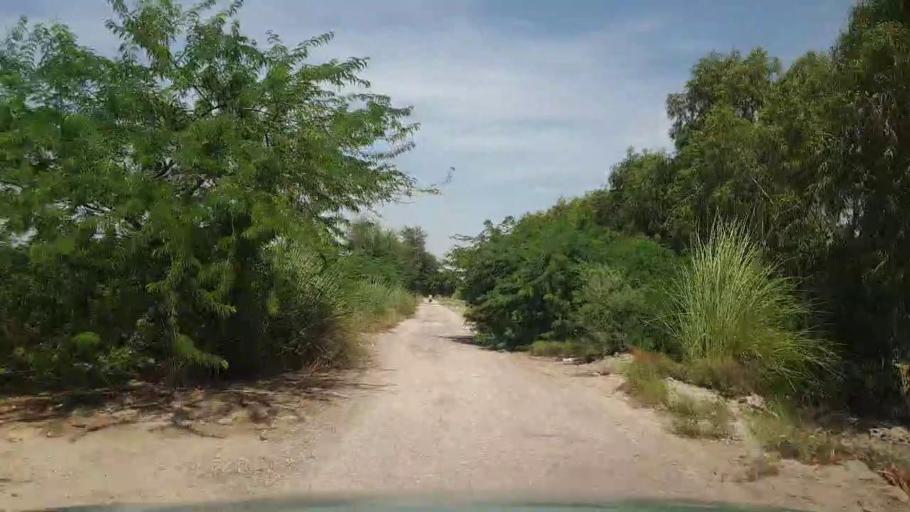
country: PK
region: Sindh
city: Bozdar
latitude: 27.0887
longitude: 69.0086
